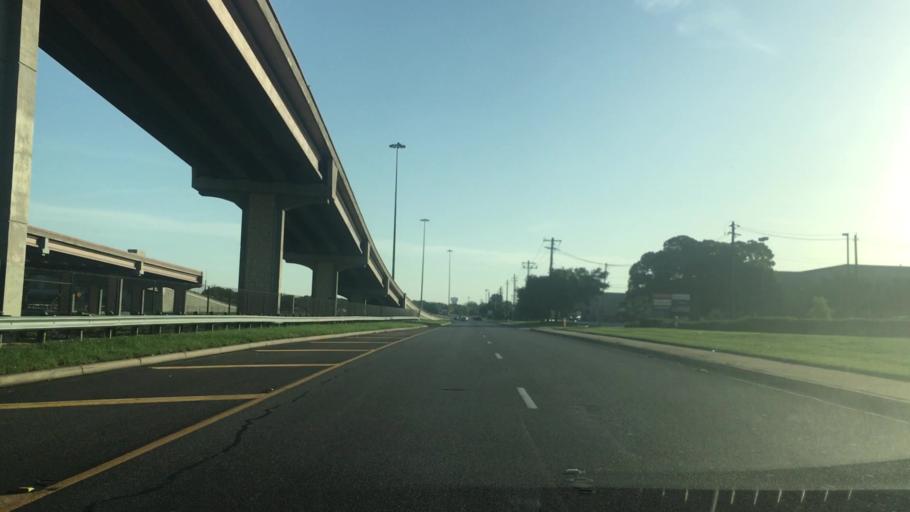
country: US
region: Texas
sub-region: Williamson County
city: Anderson Mill
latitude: 30.4686
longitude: -97.7986
